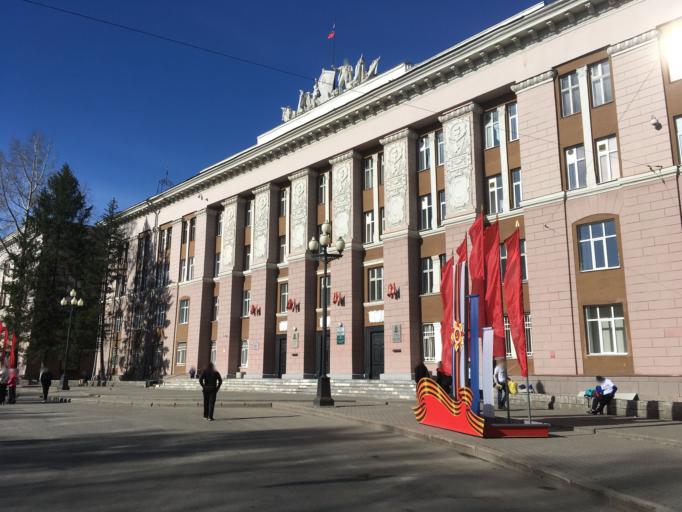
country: RU
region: Tomsk
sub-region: Tomskiy Rayon
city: Tomsk
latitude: 56.4564
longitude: 84.9511
